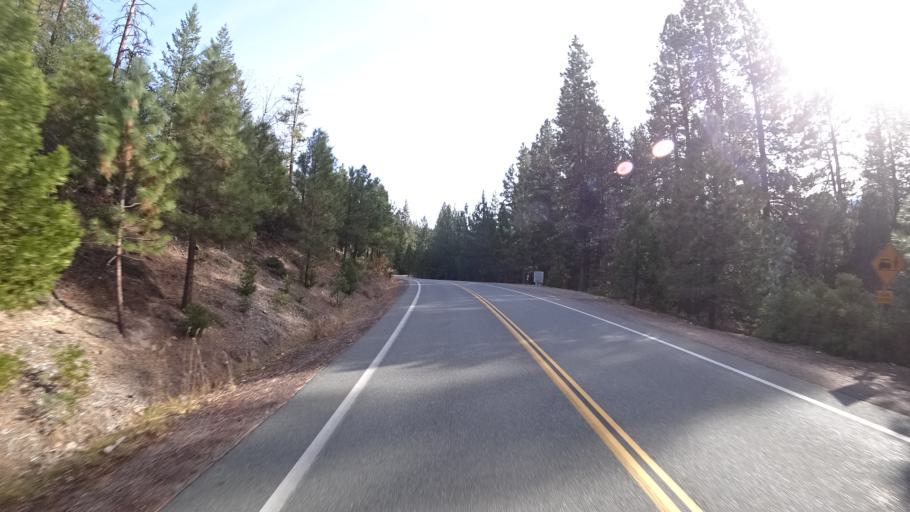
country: US
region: California
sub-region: Siskiyou County
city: Weed
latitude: 41.3981
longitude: -122.4194
